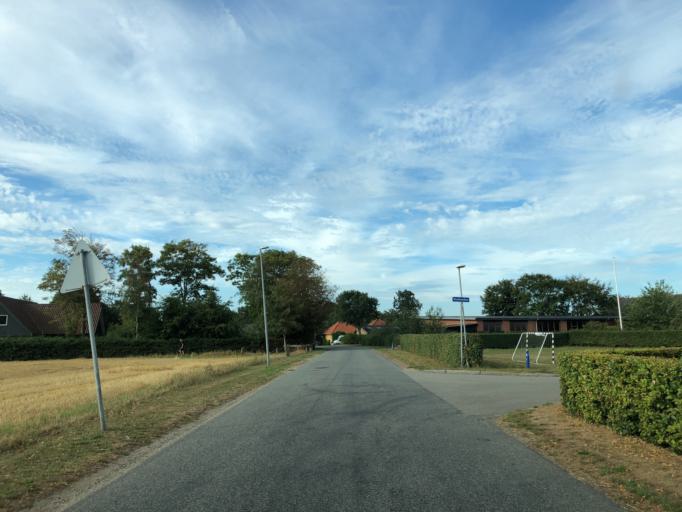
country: DK
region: Central Jutland
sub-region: Ringkobing-Skjern Kommune
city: Skjern
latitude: 56.0552
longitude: 8.4063
